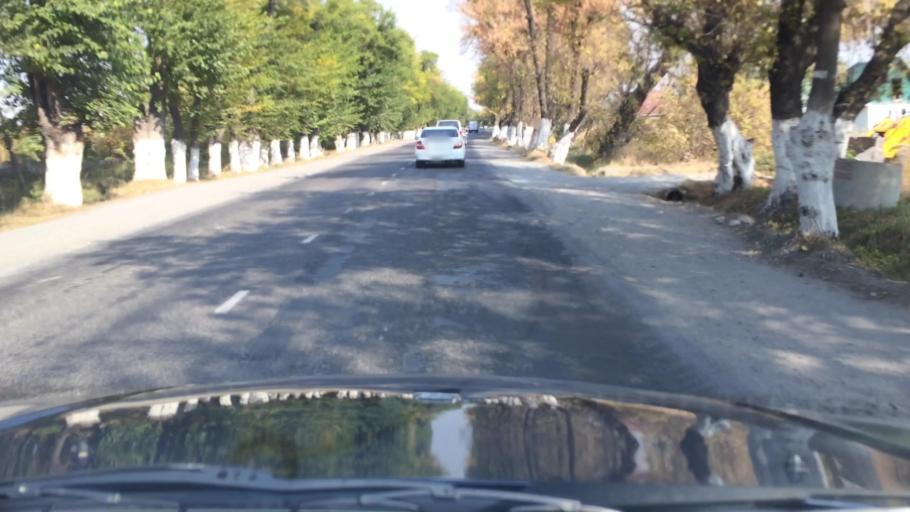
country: KG
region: Chuy
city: Lebedinovka
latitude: 42.9093
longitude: 74.6872
